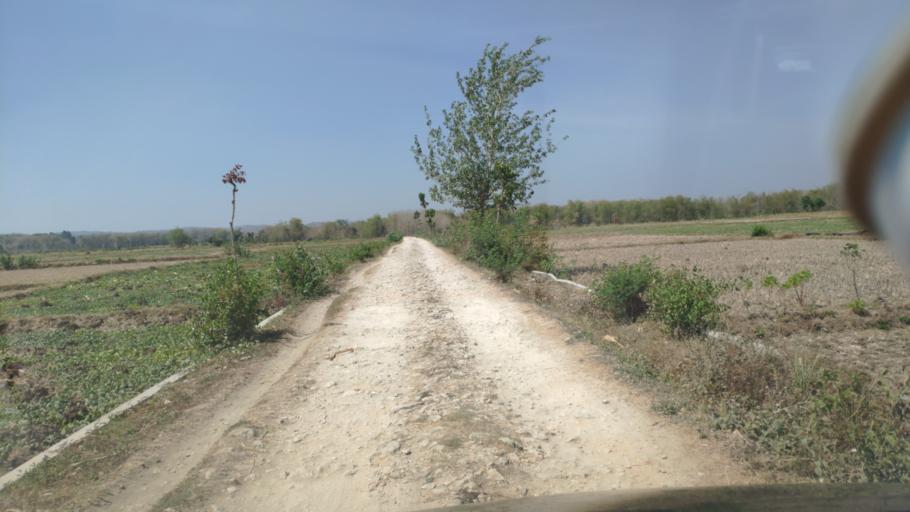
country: ID
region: Central Java
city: Mojo Wetan
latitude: -7.0308
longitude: 111.3610
